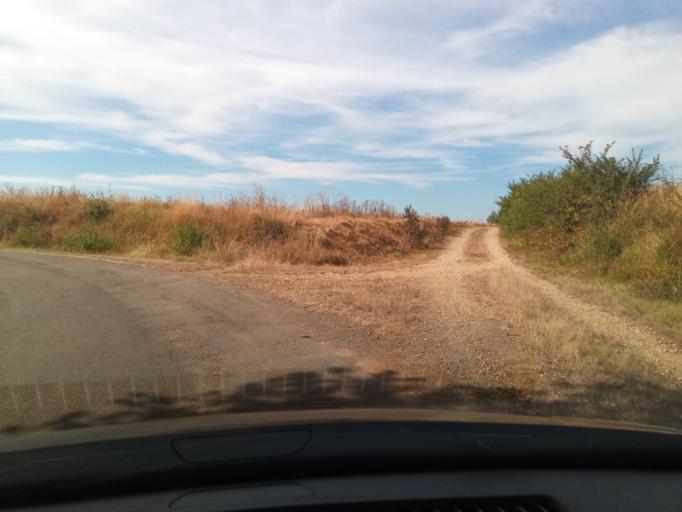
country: FR
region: Poitou-Charentes
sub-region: Departement de la Vienne
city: Chauvigny
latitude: 46.5567
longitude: 0.7416
